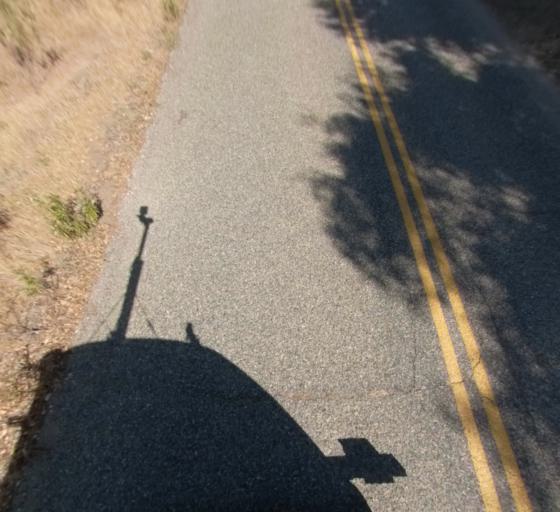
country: US
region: California
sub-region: Fresno County
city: Auberry
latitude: 37.2161
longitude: -119.3636
